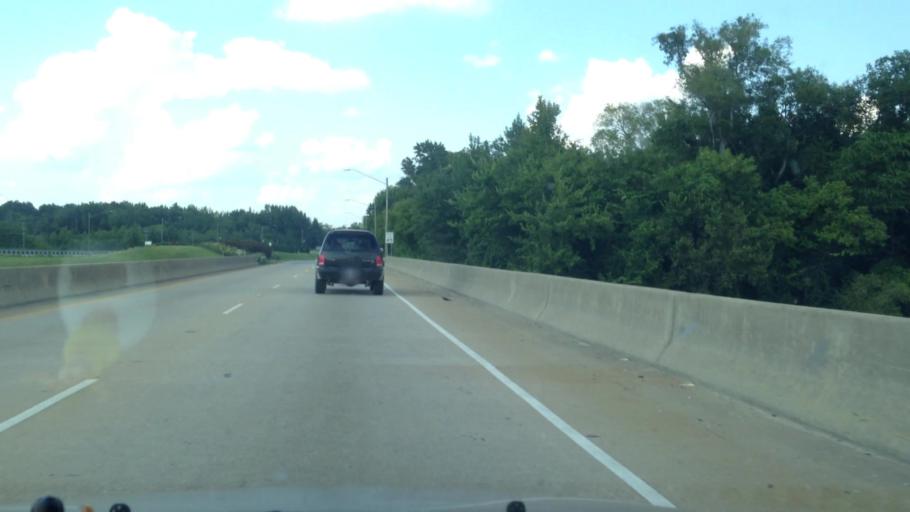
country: US
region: North Carolina
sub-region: Harnett County
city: Lillington
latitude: 35.4069
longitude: -78.8129
